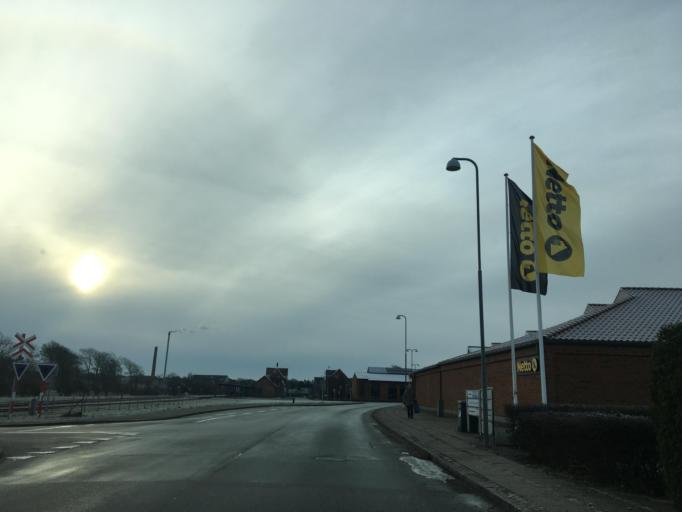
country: DK
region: North Denmark
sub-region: Thisted Kommune
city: Hurup
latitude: 56.7533
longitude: 8.4183
